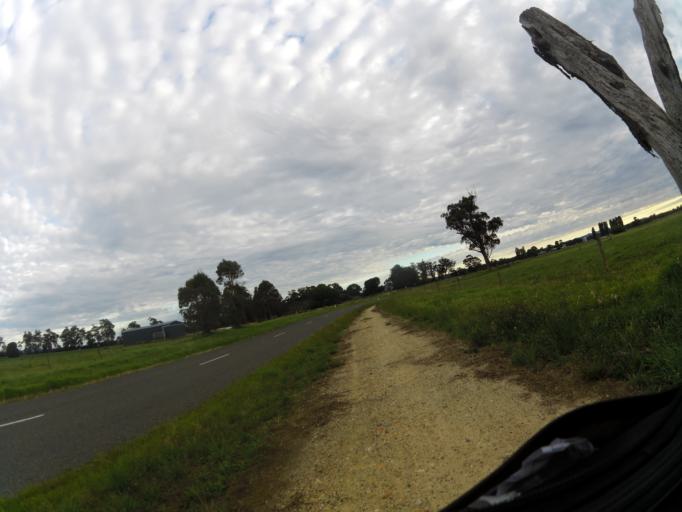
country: AU
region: Victoria
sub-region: East Gippsland
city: Lakes Entrance
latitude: -37.7252
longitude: 148.4405
